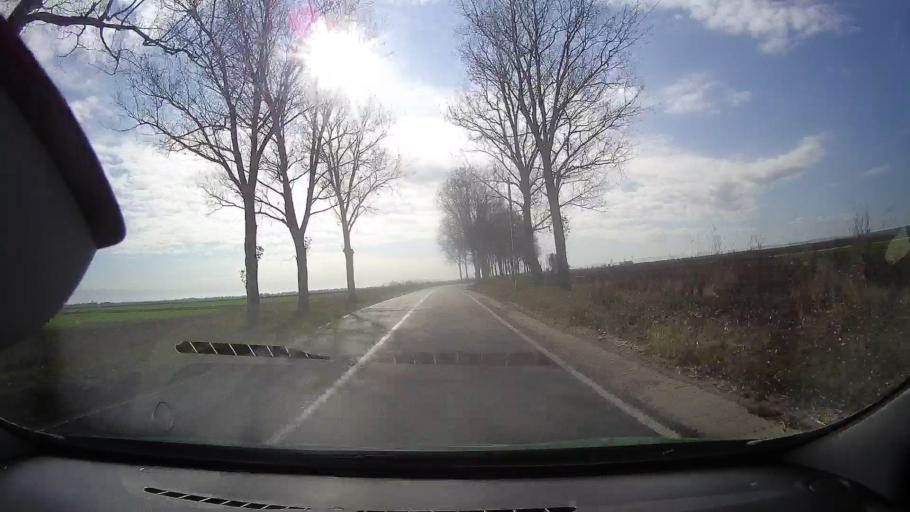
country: RO
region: Tulcea
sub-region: Comuna Valea Nucarilor
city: Agighiol
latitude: 44.9972
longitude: 28.8865
